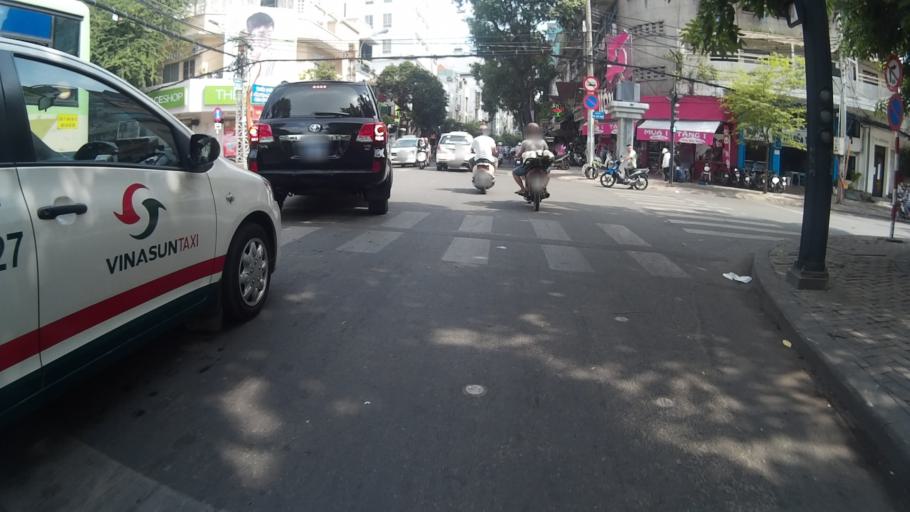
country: VN
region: Ho Chi Minh City
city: Quan Ba
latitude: 10.7683
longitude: 106.6896
